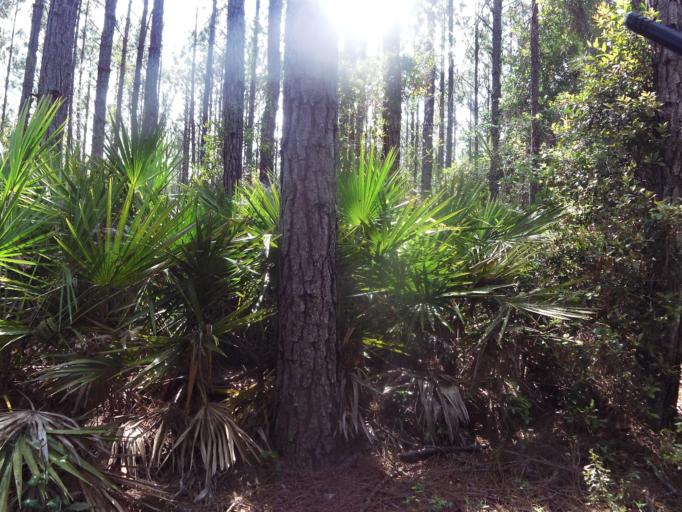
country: US
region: Florida
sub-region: Nassau County
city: Yulee
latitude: 30.4899
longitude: -81.4983
